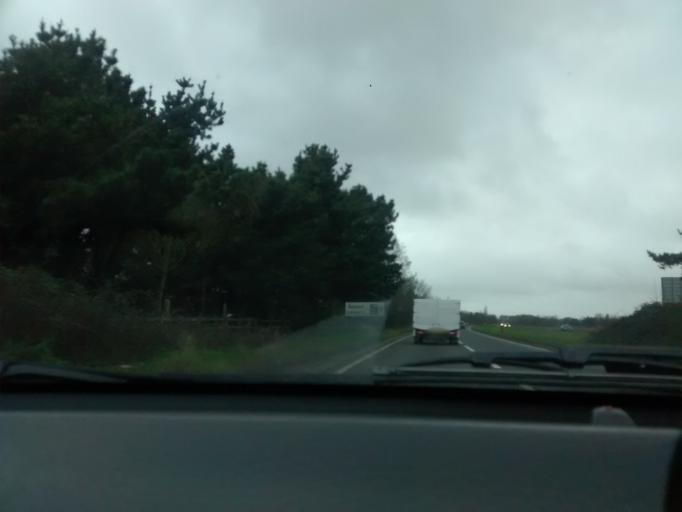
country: GB
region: England
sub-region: Suffolk
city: Felixstowe
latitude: 51.9802
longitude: 1.3280
